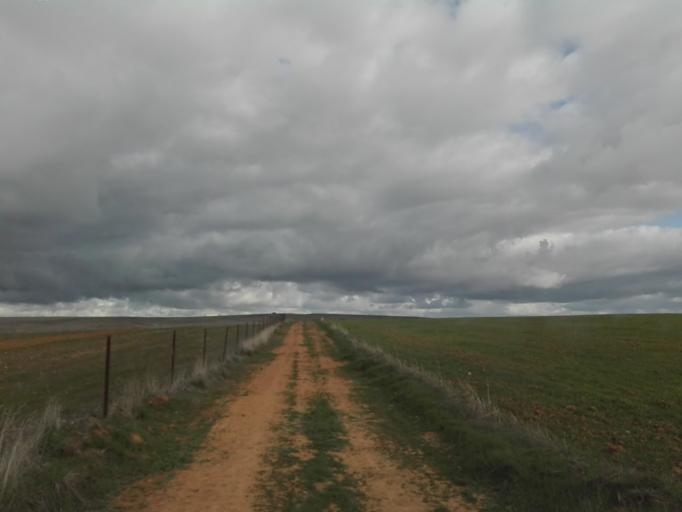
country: ES
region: Extremadura
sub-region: Provincia de Badajoz
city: Llerena
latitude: 38.2919
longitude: -6.0032
